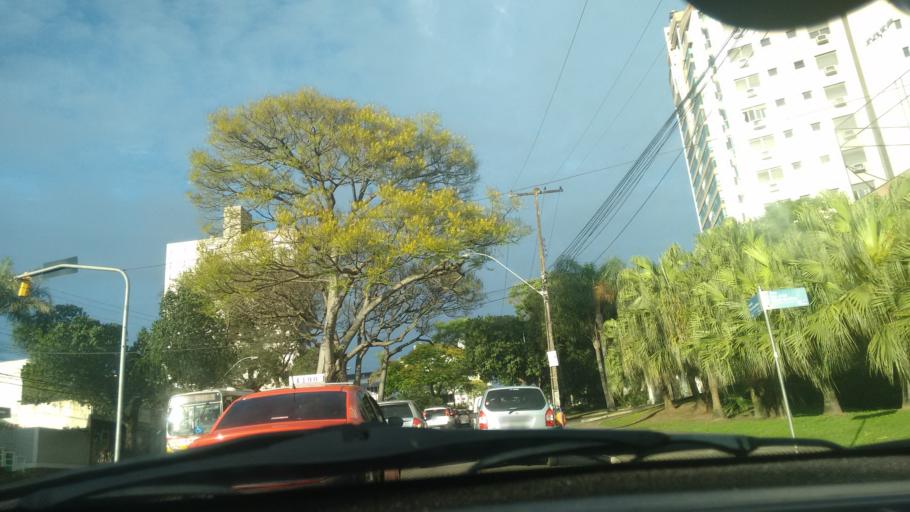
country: BR
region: Rio Grande do Sul
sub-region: Porto Alegre
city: Porto Alegre
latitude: -30.0195
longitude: -51.1780
